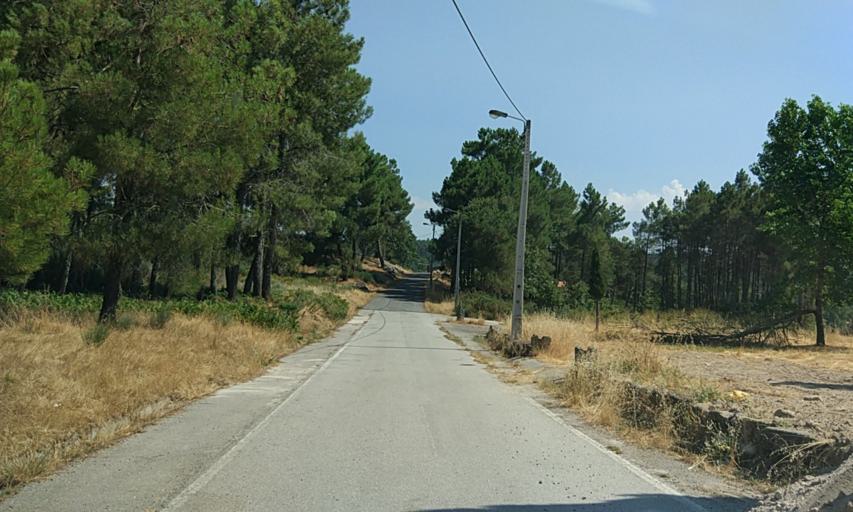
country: PT
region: Vila Real
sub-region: Murca
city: Murca
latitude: 41.3512
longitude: -7.4860
